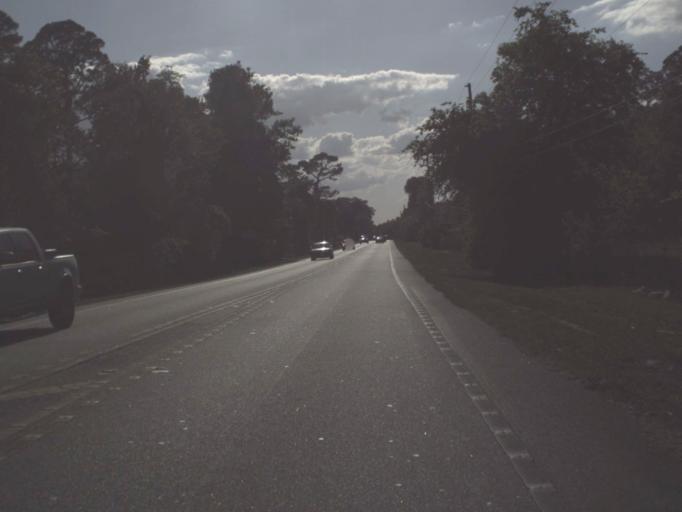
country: US
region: Florida
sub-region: Seminole County
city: Heathrow
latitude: 28.8155
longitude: -81.4269
